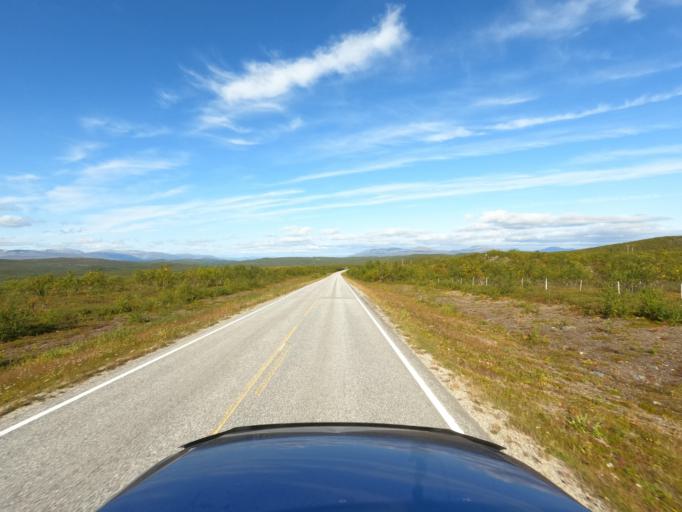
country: NO
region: Finnmark Fylke
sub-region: Karasjok
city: Karasjohka
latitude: 69.7241
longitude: 25.2364
